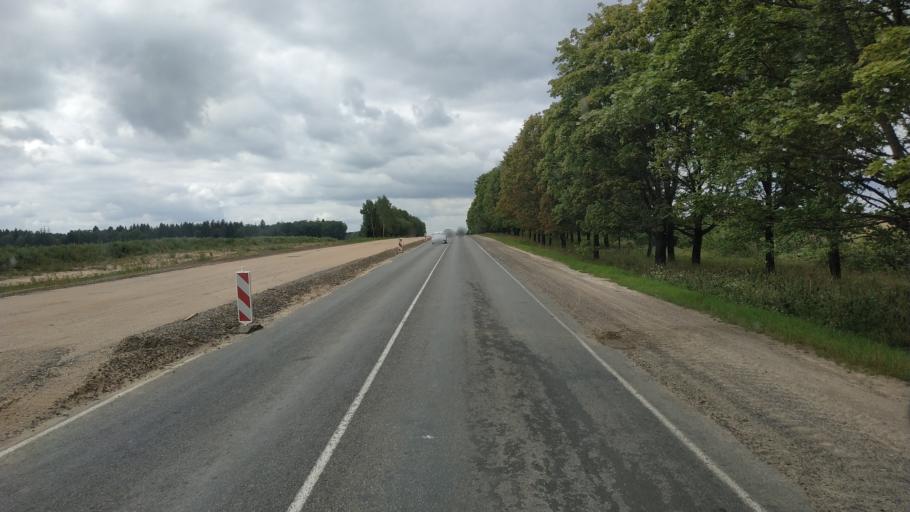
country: BY
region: Mogilev
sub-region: Mahilyowski Rayon
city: Kadino
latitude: 53.8696
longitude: 30.4641
